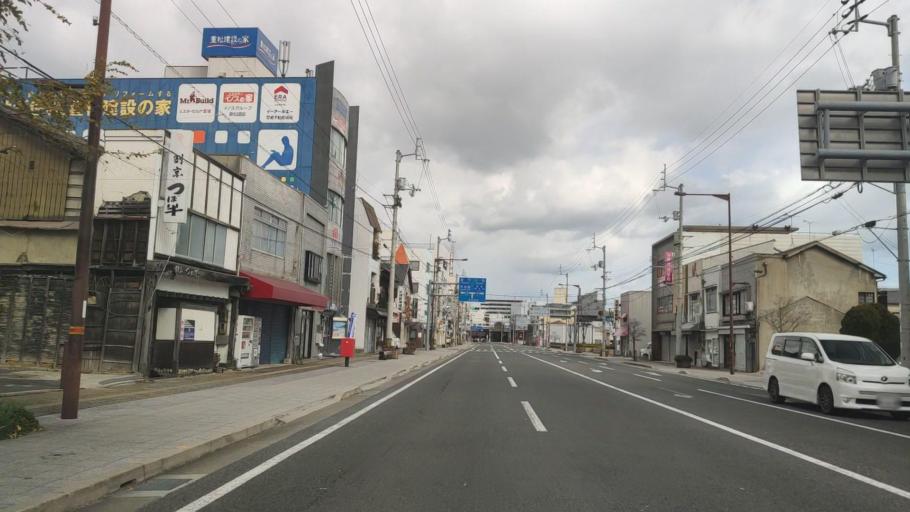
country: JP
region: Ehime
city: Hojo
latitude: 34.0632
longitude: 132.9967
